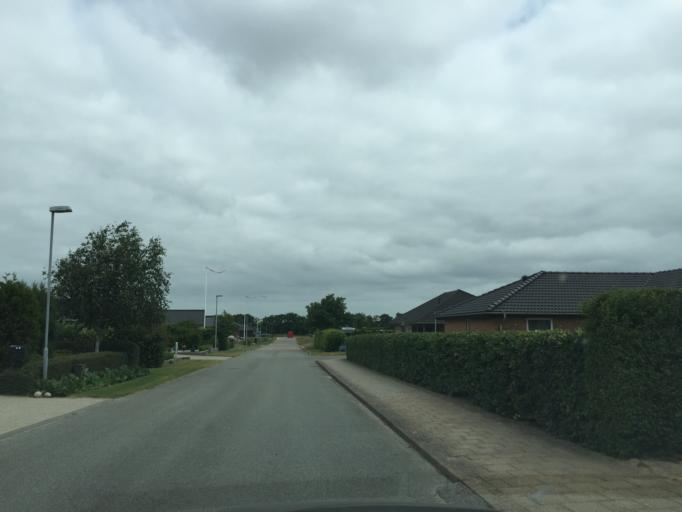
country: DK
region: South Denmark
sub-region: Tonder Kommune
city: Sherrebek
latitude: 55.1519
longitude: 8.7503
